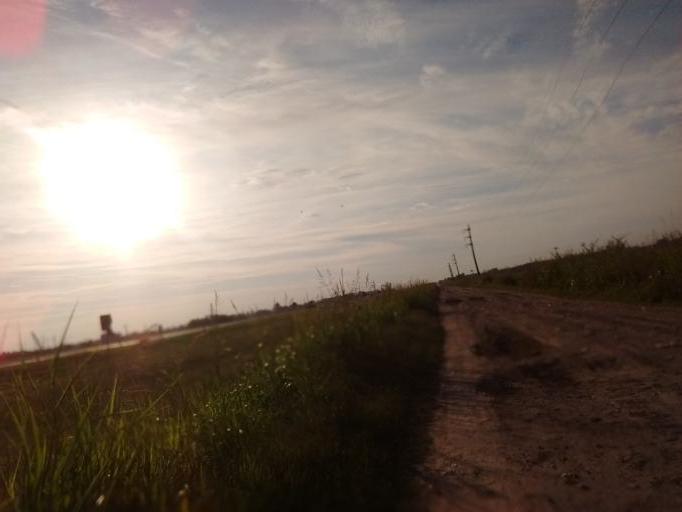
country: AR
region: Santa Fe
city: Roldan
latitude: -32.9308
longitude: -60.8683
